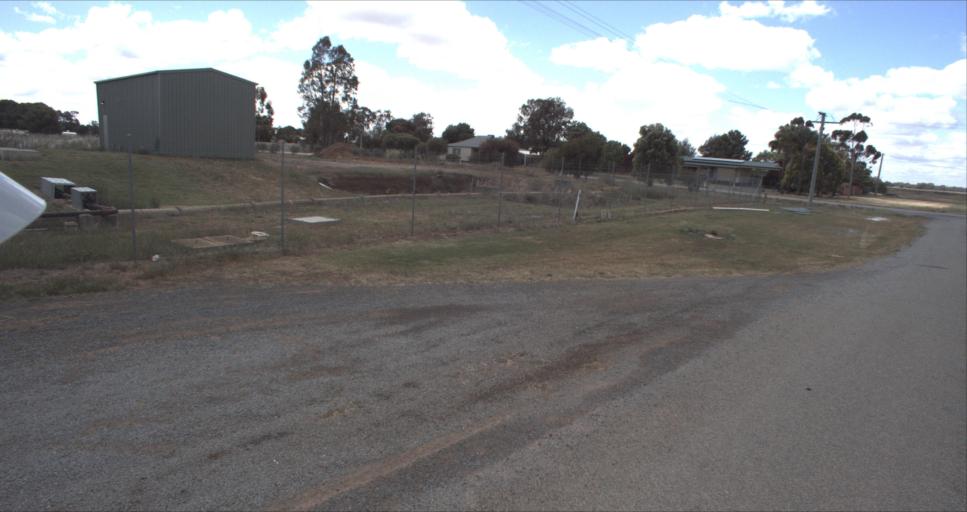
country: AU
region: New South Wales
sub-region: Murrumbidgee Shire
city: Darlington Point
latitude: -34.5141
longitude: 146.1835
